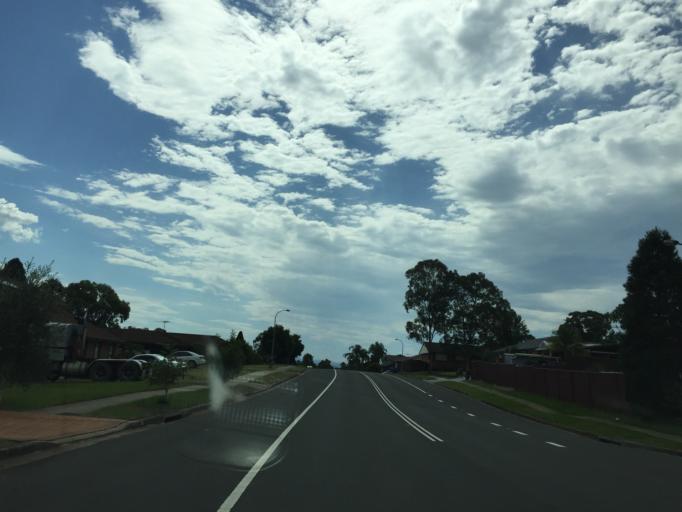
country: AU
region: New South Wales
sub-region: Blacktown
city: Mount Druitt
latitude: -33.8008
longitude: 150.7874
